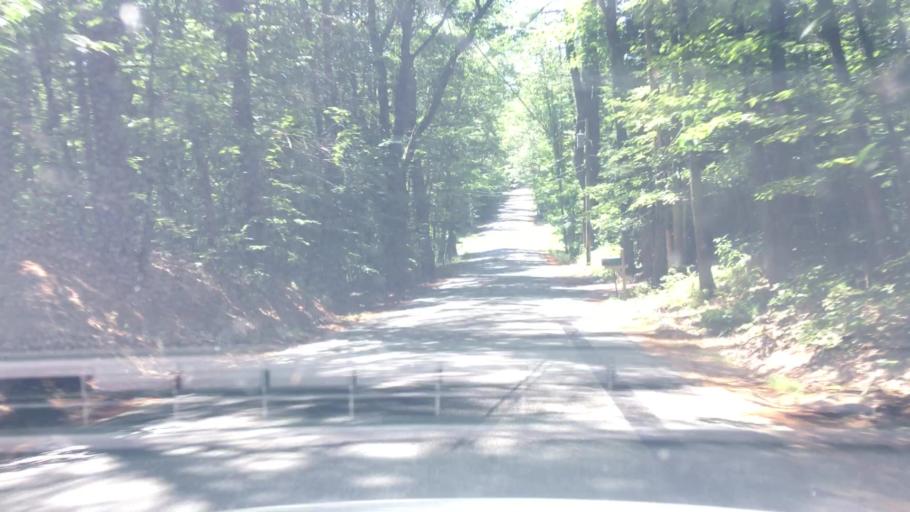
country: US
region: New Hampshire
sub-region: Merrimack County
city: Hopkinton
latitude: 43.2087
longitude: -71.6701
